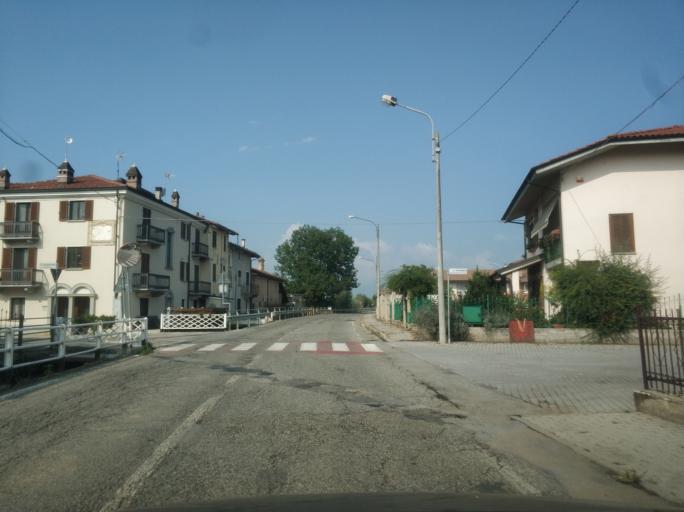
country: IT
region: Piedmont
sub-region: Provincia di Cuneo
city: Montanera
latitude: 44.5120
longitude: 7.6453
